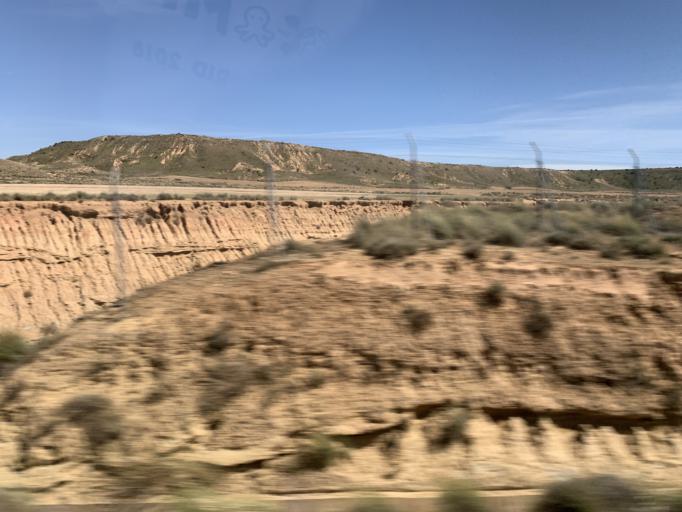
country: ES
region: Aragon
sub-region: Provincia de Huesca
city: Candasnos
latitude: 41.5636
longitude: 0.0867
